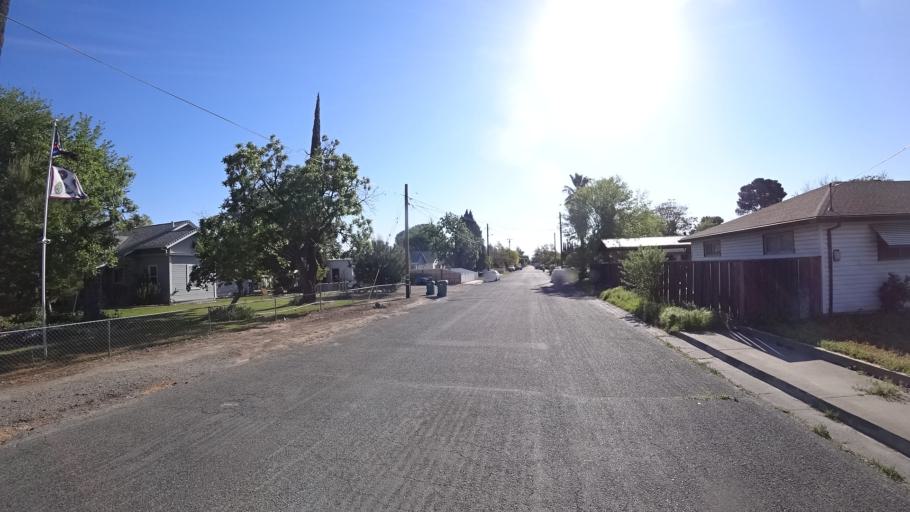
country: US
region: California
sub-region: Glenn County
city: Orland
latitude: 39.7426
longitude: -122.1946
